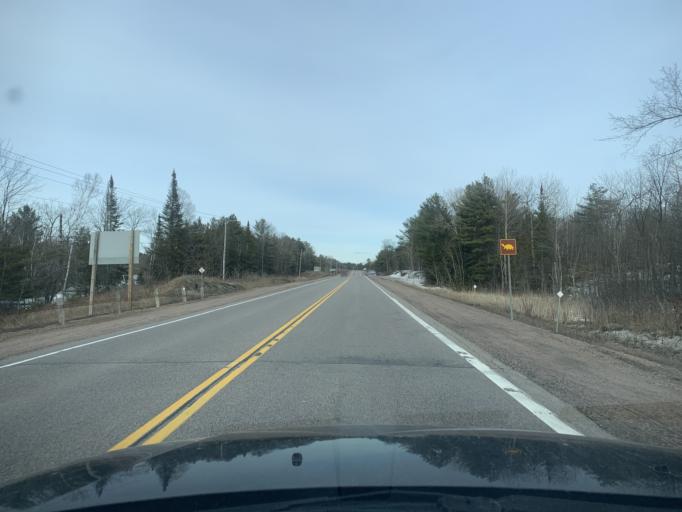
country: CA
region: Ontario
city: Greater Napanee
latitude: 44.6696
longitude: -77.0653
